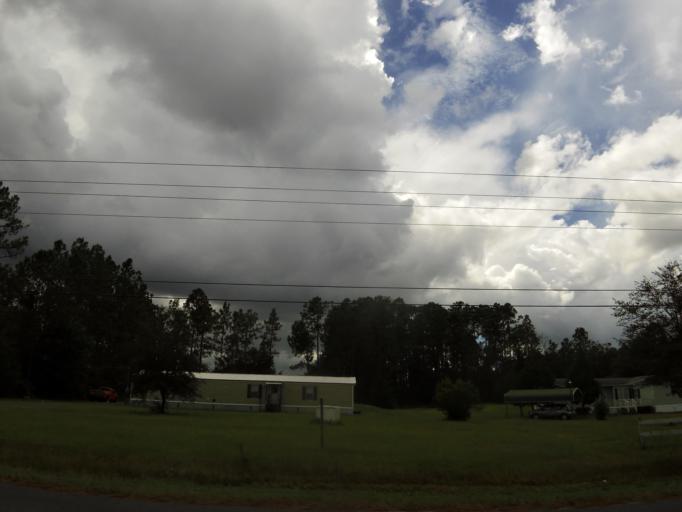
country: US
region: Florida
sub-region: Clay County
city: Middleburg
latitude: 30.0687
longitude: -81.9264
